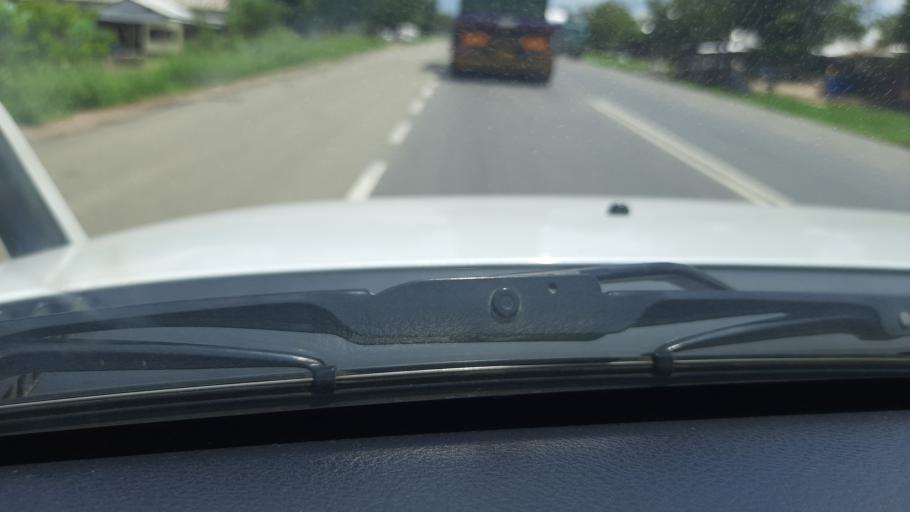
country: TZ
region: Pwani
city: Chalinze
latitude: -6.6374
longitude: 38.3423
